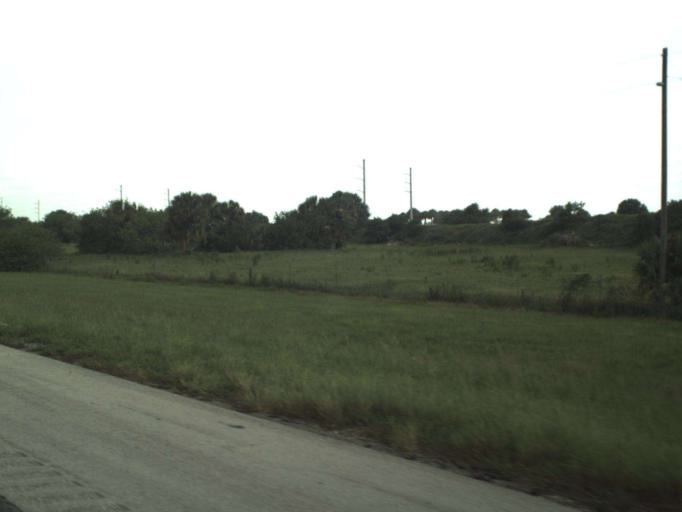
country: US
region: Florida
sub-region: Saint Lucie County
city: Lakewood Park
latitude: 27.5400
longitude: -80.4659
